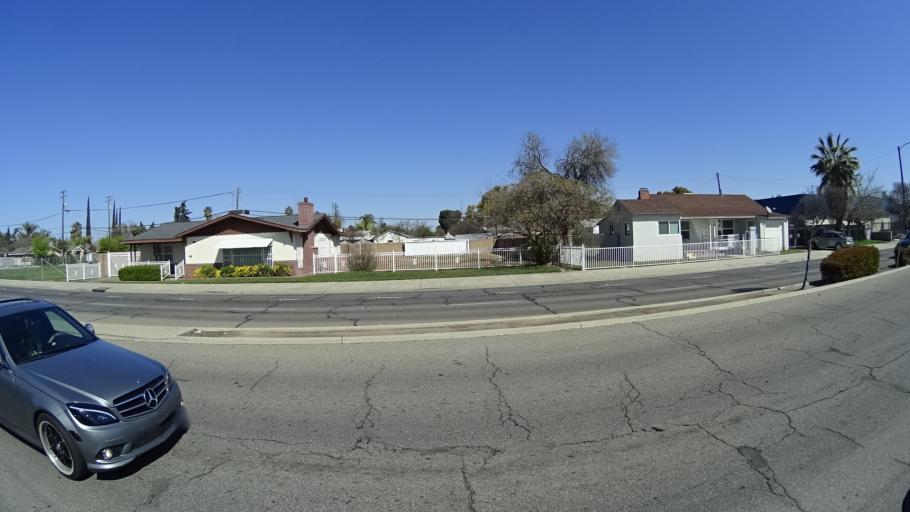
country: US
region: California
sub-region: Fresno County
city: Fresno
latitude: 36.7649
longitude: -119.7740
